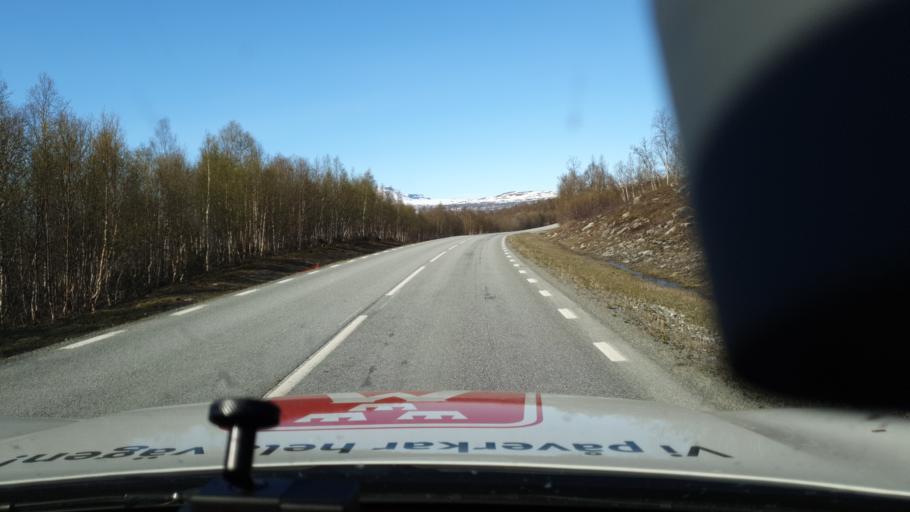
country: NO
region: Nordland
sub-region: Rana
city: Mo i Rana
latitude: 65.9885
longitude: 15.0684
